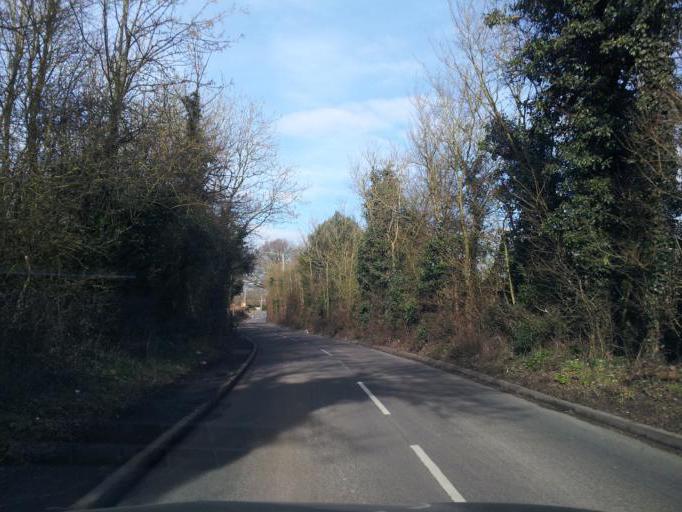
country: GB
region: England
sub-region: Hertfordshire
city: Shenley AV
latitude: 51.7450
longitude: -0.2775
